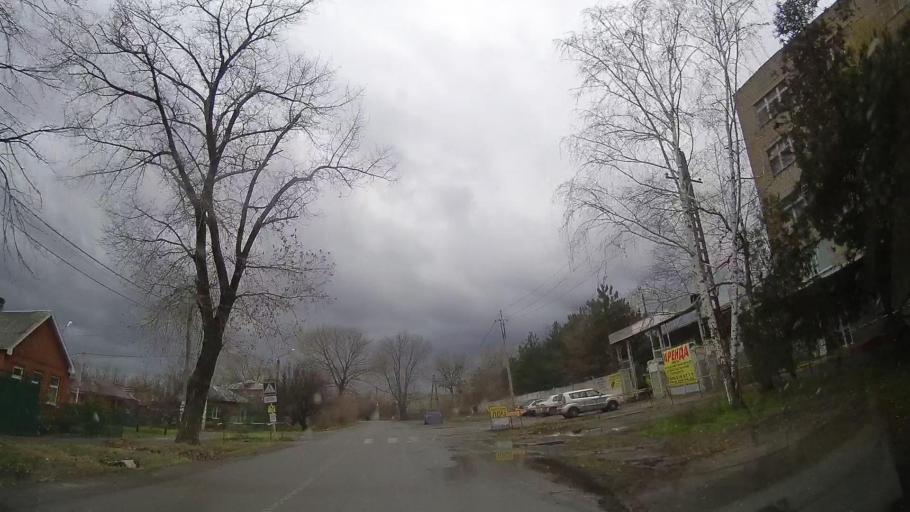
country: RU
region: Rostov
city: Bataysk
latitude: 47.1128
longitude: 39.7394
